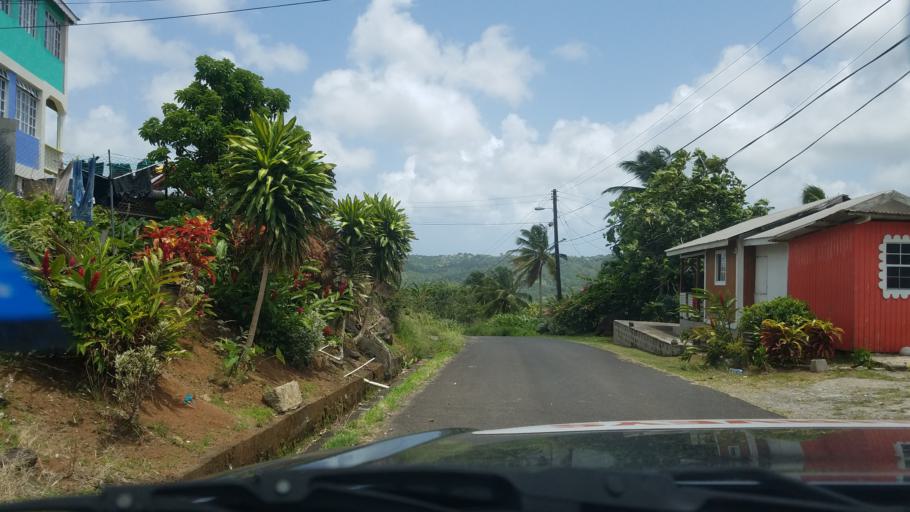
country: LC
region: Castries Quarter
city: Bisee
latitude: 13.9890
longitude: -60.9229
